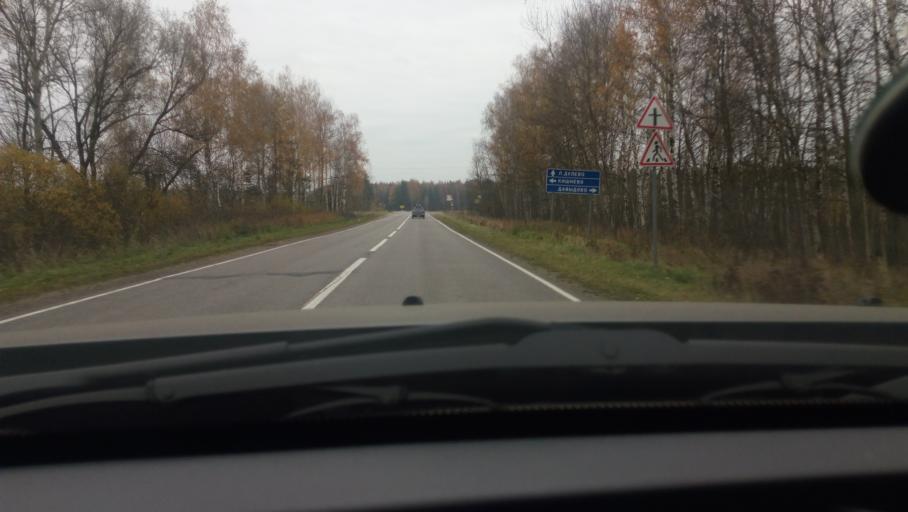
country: RU
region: Moskovskaya
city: Drezna
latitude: 55.7069
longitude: 38.8667
